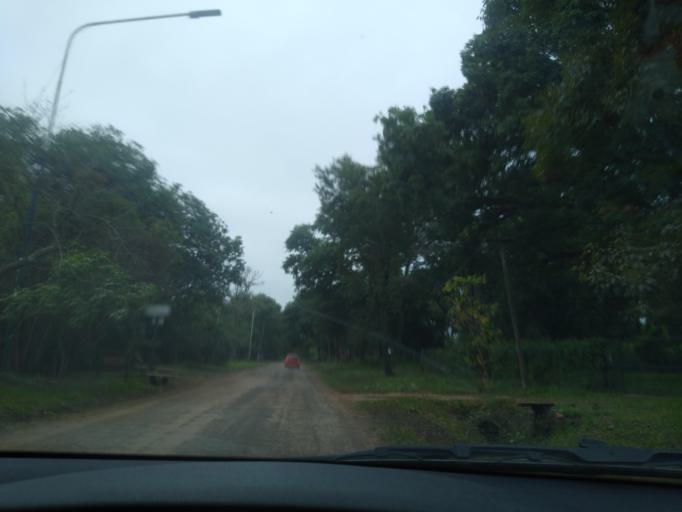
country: AR
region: Chaco
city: Colonia Benitez
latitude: -27.3338
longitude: -58.9549
